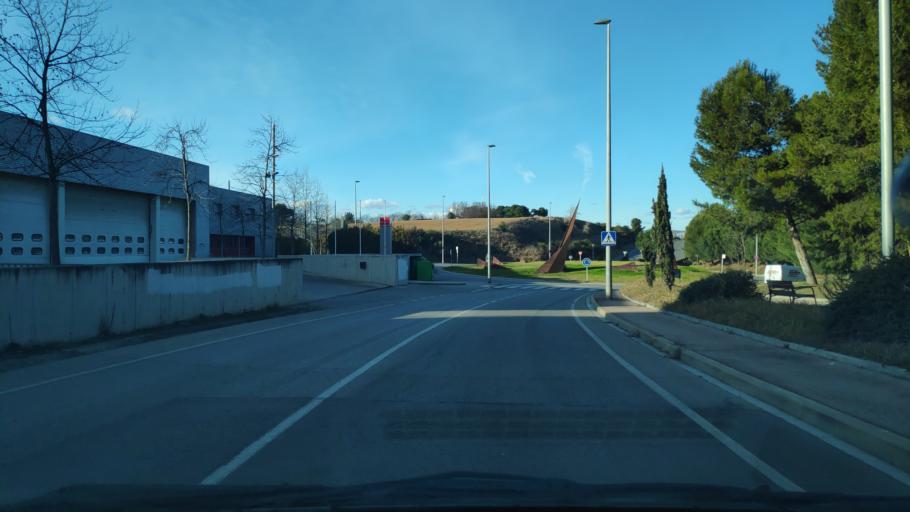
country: ES
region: Catalonia
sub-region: Provincia de Barcelona
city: Mollet del Valles
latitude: 41.5366
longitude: 2.2025
